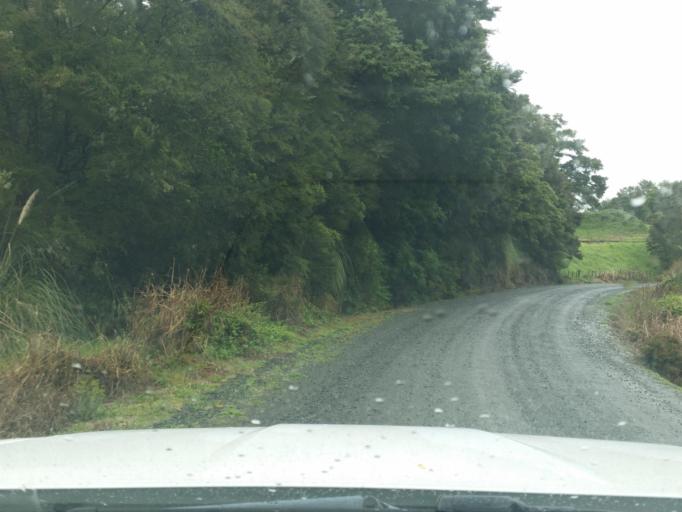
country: NZ
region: Northland
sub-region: Kaipara District
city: Dargaville
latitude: -35.7820
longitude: 173.9552
